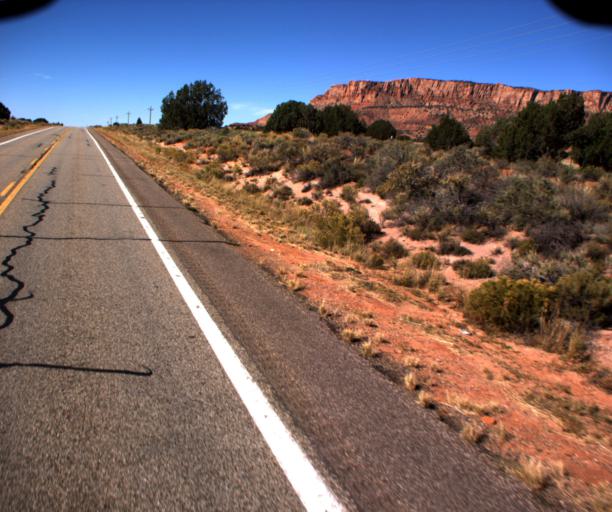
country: US
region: Arizona
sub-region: Mohave County
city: Colorado City
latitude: 36.8580
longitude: -112.7693
